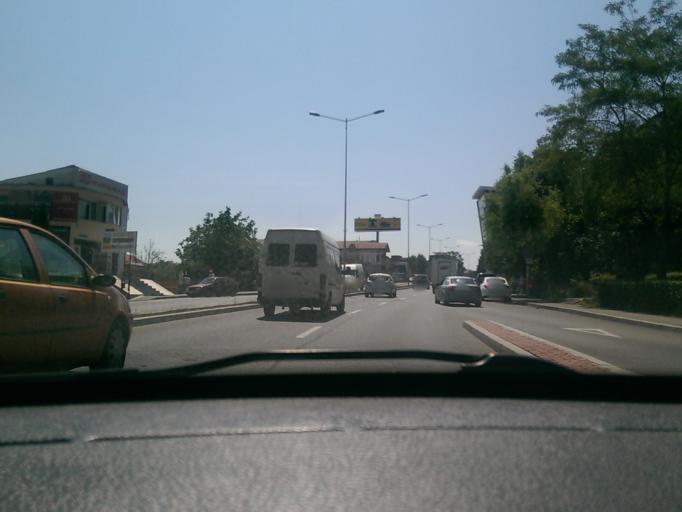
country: RO
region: Cluj
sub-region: Municipiul Cluj-Napoca
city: Cluj-Napoca
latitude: 46.7554
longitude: 23.5961
